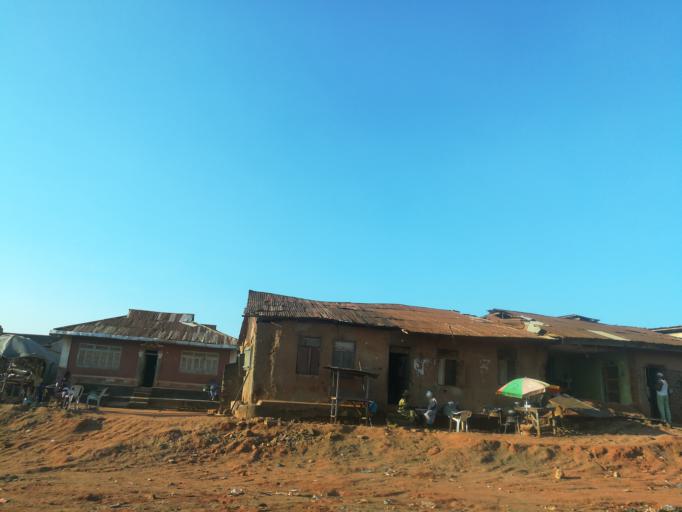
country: NG
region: Lagos
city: Ikorodu
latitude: 6.5921
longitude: 3.5159
